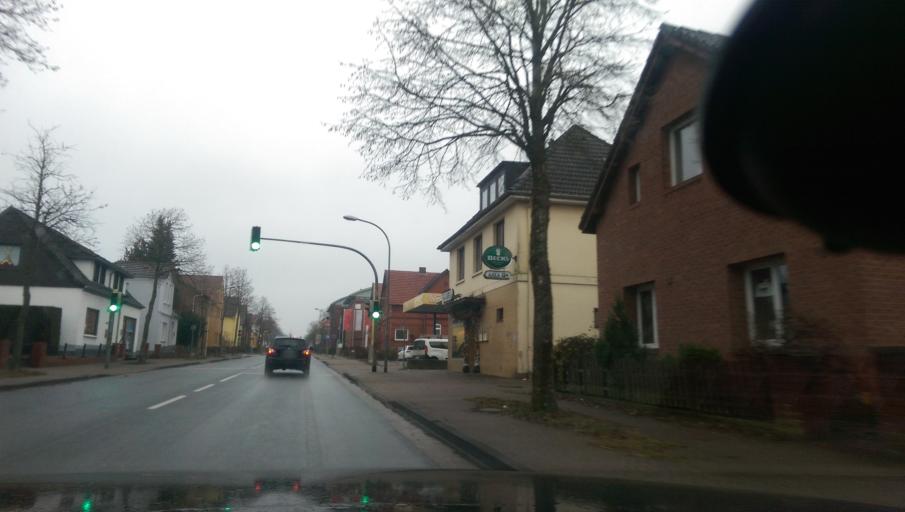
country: DE
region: Lower Saxony
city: Verden
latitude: 52.9240
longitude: 9.2433
